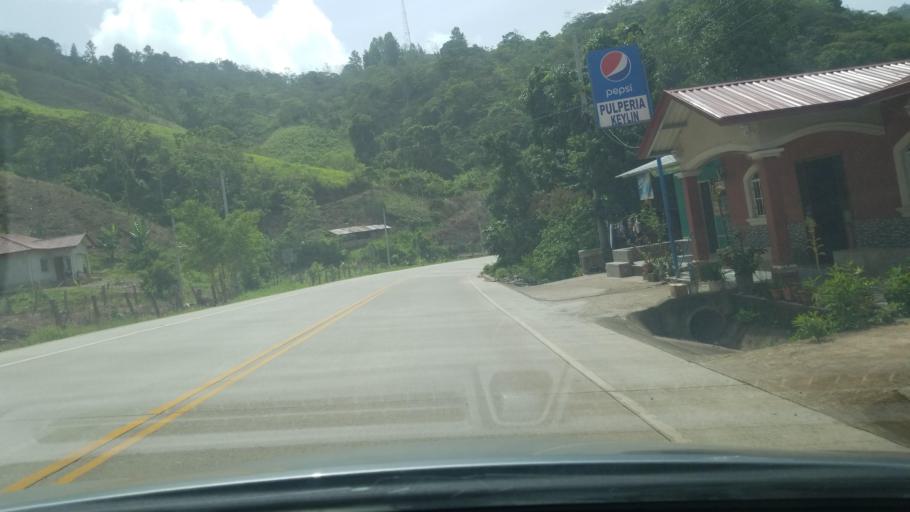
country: HN
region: Copan
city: Buenos Aires
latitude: 14.9320
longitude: -88.9637
